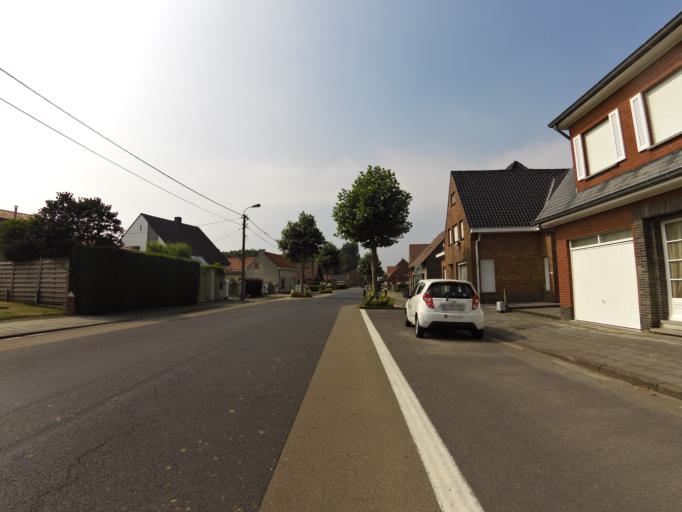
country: BE
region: Flanders
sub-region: Provincie West-Vlaanderen
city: Ichtegem
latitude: 51.1192
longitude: 3.0373
